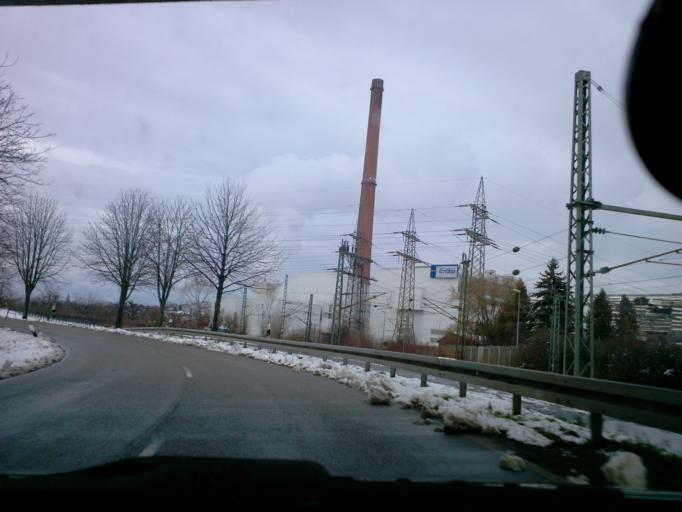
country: DE
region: Baden-Wuerttemberg
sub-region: Regierungsbezirk Stuttgart
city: Walheim
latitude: 49.0158
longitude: 9.1549
